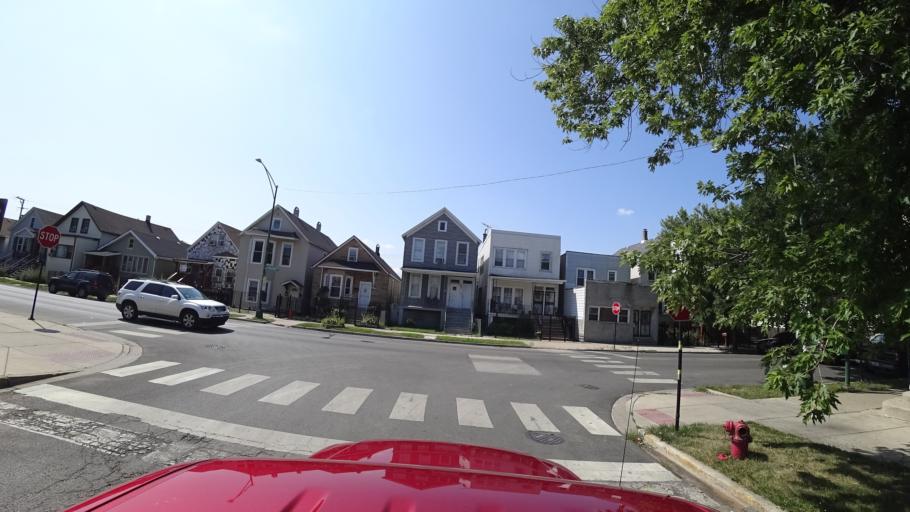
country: US
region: Illinois
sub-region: Cook County
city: Chicago
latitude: 41.8230
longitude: -87.6922
